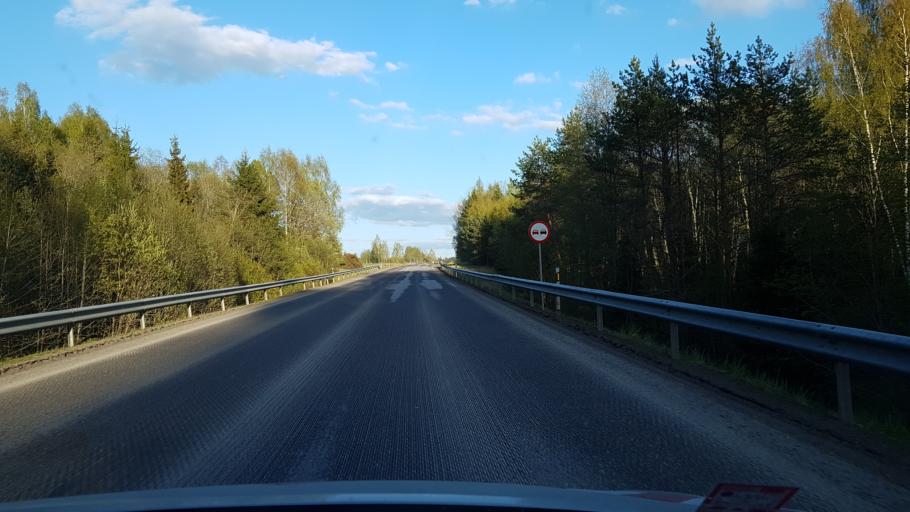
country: EE
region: Vorumaa
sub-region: Voru linn
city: Voru
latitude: 57.7638
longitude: 27.1947
